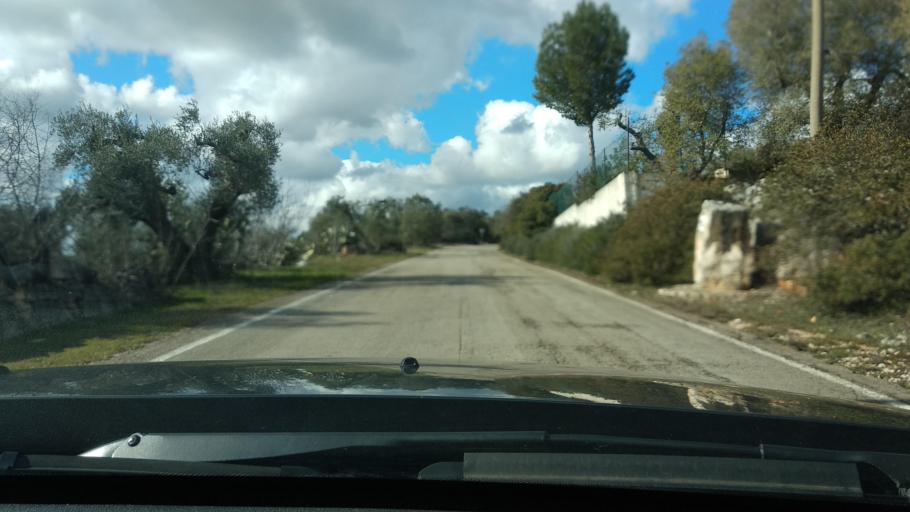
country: IT
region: Apulia
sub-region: Provincia di Brindisi
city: Casalini
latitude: 40.6913
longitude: 17.4757
